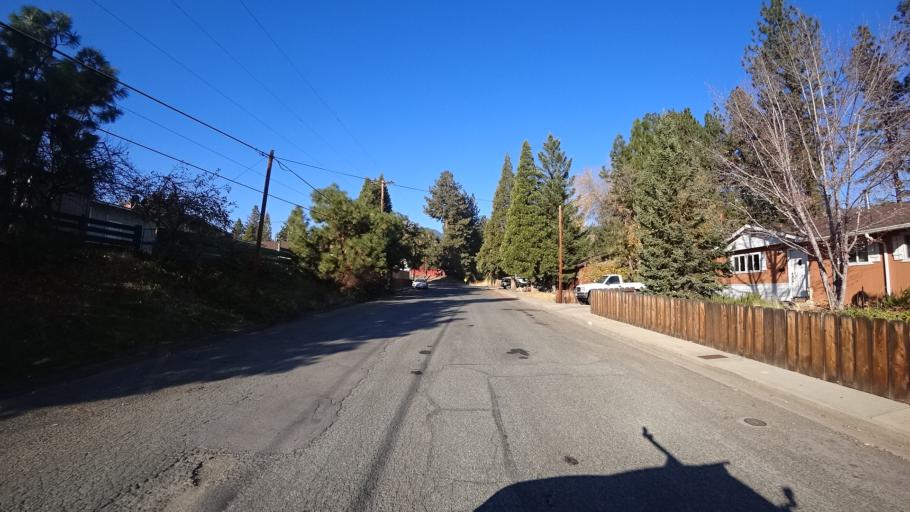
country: US
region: California
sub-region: Siskiyou County
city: Yreka
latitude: 41.7392
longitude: -122.6448
